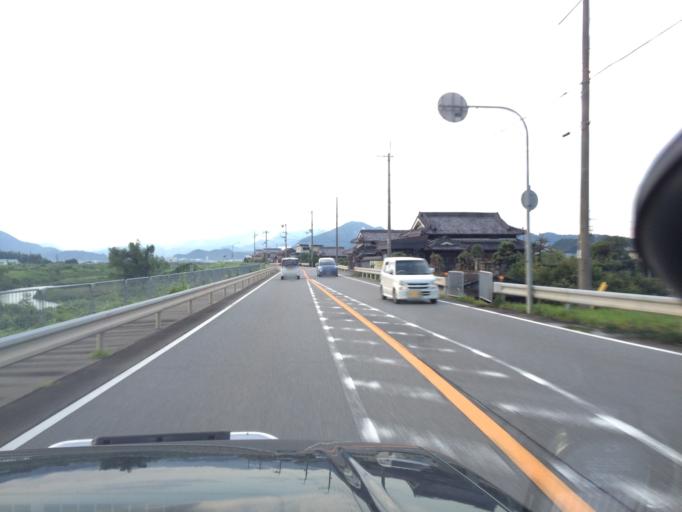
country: JP
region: Hyogo
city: Nishiwaki
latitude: 35.1393
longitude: 135.0276
